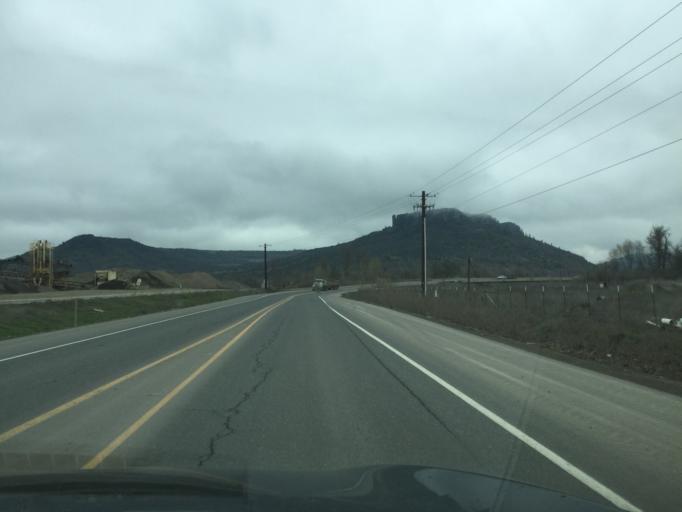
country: US
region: Oregon
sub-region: Jackson County
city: Central Point
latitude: 42.4237
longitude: -122.9586
